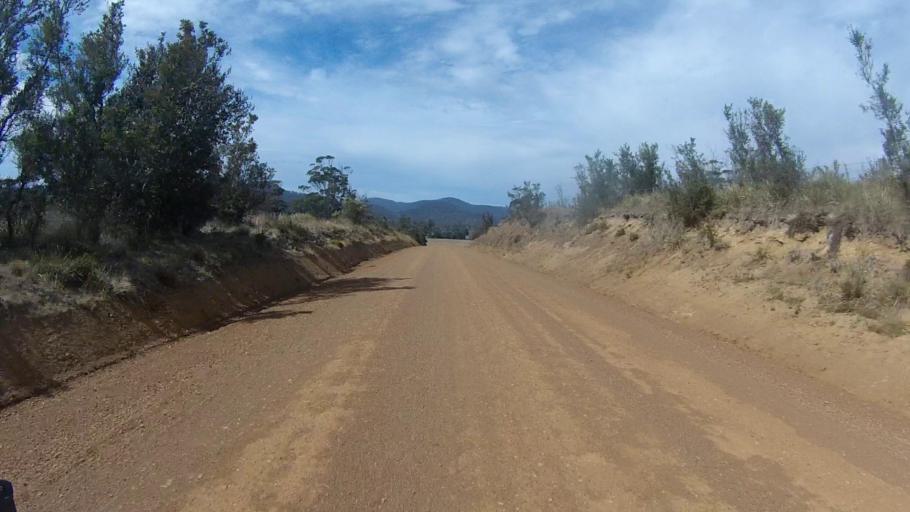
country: AU
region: Tasmania
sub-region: Sorell
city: Sorell
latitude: -42.6329
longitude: 147.9011
